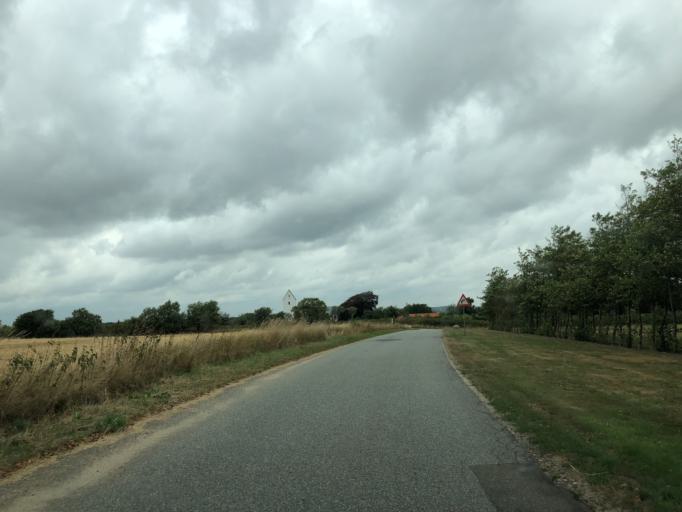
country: DK
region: Central Jutland
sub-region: Ringkobing-Skjern Kommune
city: Videbaek
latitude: 56.1097
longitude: 8.4995
